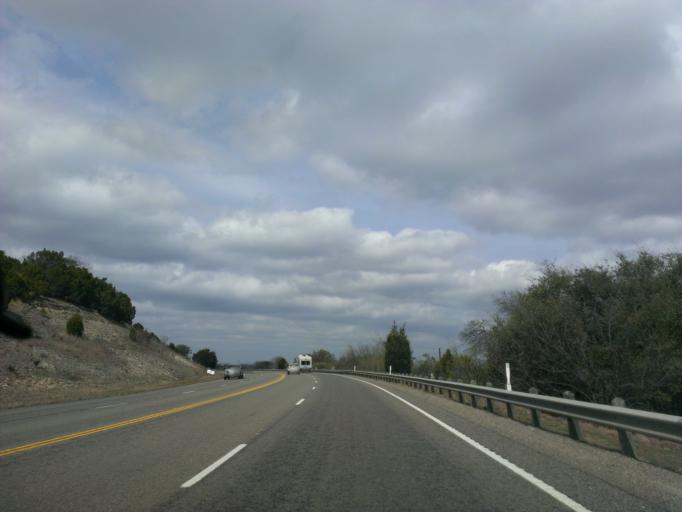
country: US
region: Texas
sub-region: Travis County
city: Briarcliff
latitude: 30.4520
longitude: -98.1489
